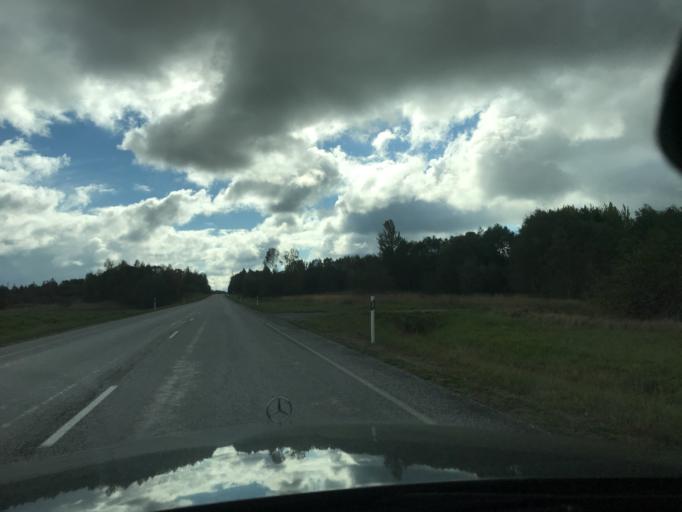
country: RU
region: Pskov
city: Pechory
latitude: 57.7040
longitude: 27.3237
